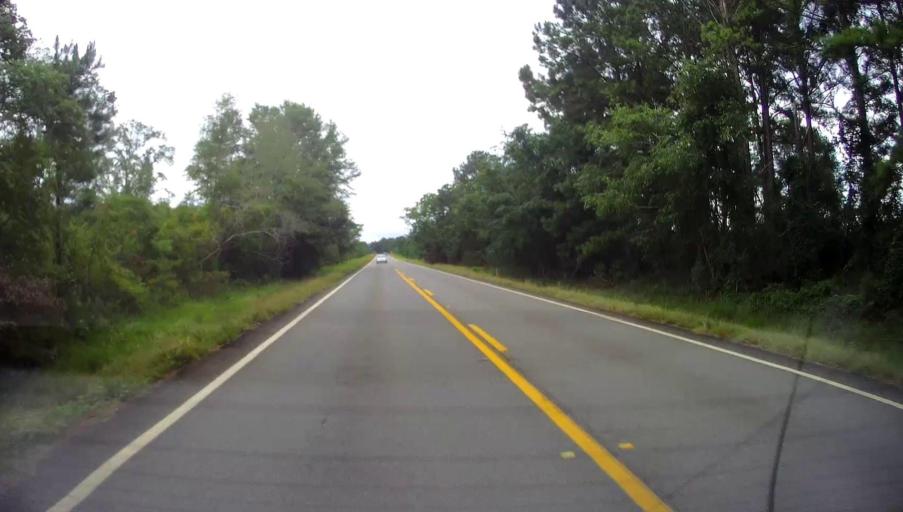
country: US
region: Georgia
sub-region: Marion County
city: Buena Vista
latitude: 32.2740
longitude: -84.4340
